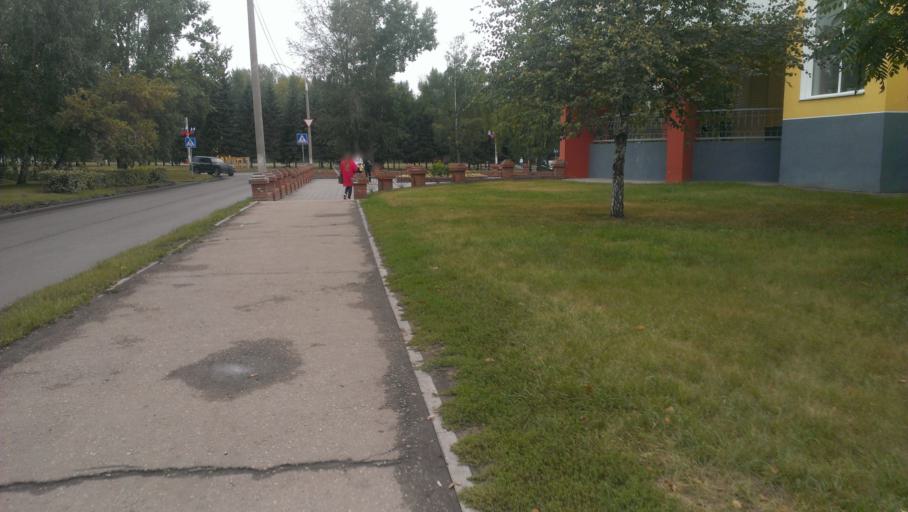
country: RU
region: Altai Krai
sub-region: Gorod Barnaulskiy
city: Barnaul
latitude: 53.3664
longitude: 83.6891
